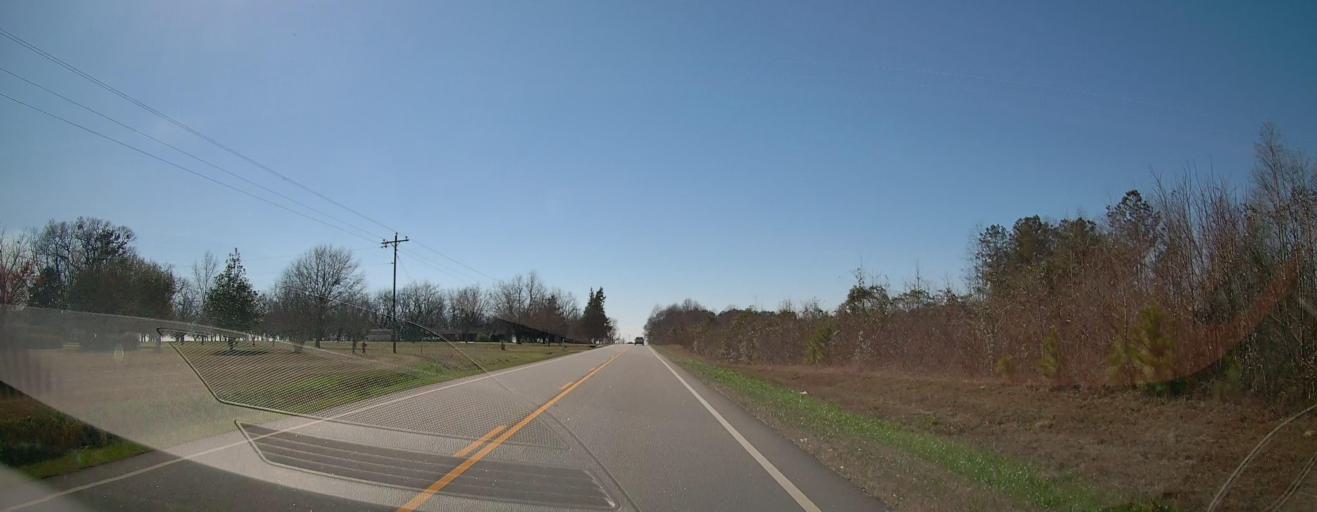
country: US
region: Georgia
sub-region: Dooly County
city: Unadilla
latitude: 32.3386
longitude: -83.8112
